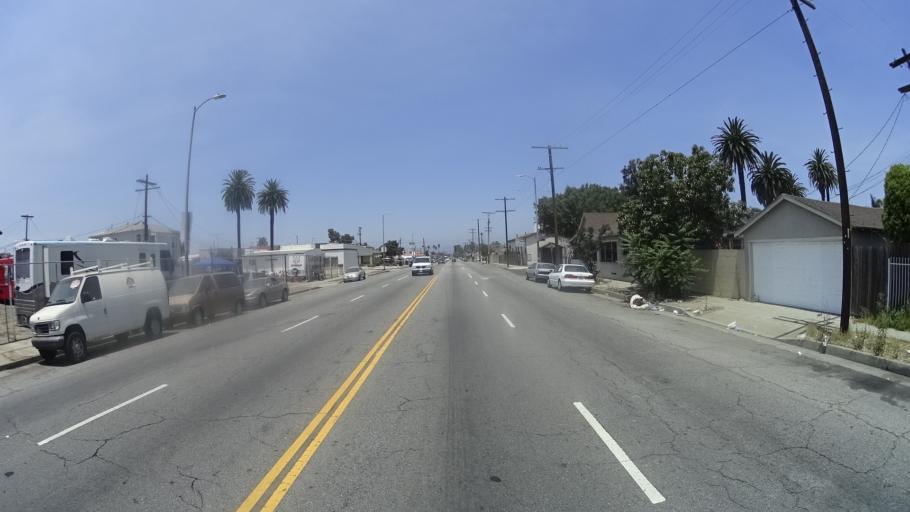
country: US
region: California
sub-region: Los Angeles County
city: Westmont
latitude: 33.9621
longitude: -118.3003
